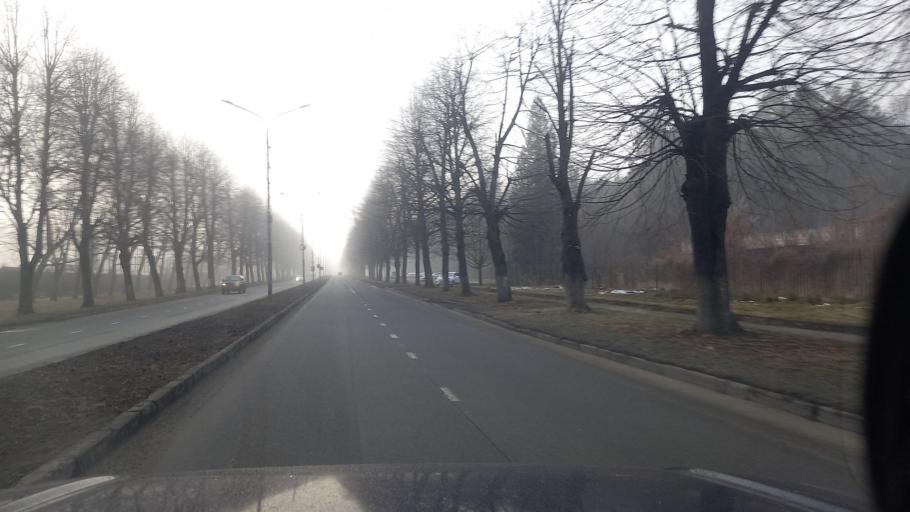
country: RU
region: North Ossetia
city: Vladikavkaz
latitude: 42.9878
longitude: 44.6749
